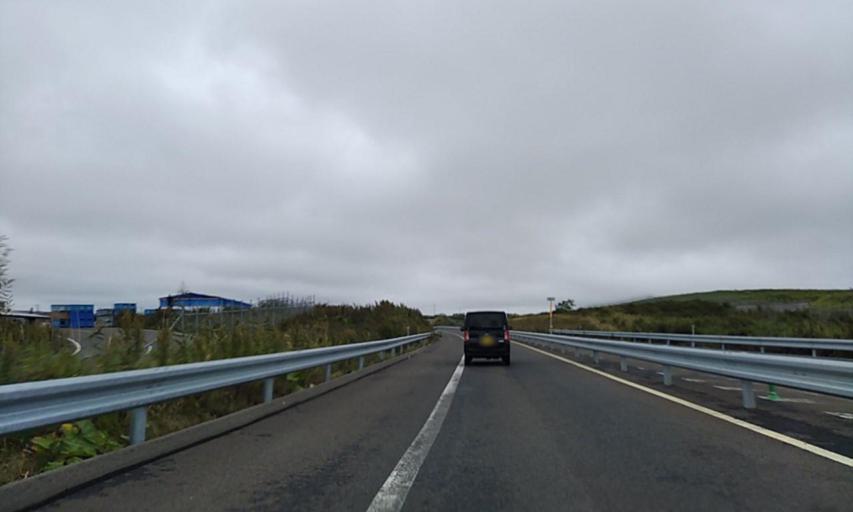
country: JP
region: Hokkaido
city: Nemuro
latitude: 43.3102
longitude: 145.5416
